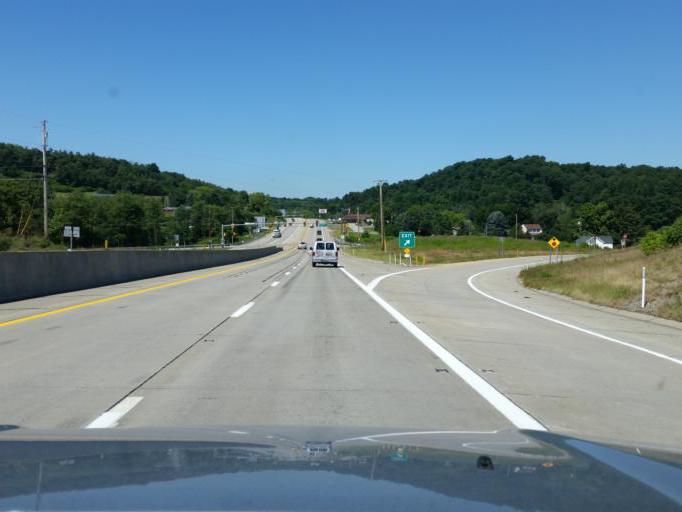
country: US
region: Pennsylvania
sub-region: Indiana County
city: Blairsville
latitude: 40.4213
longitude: -79.3421
